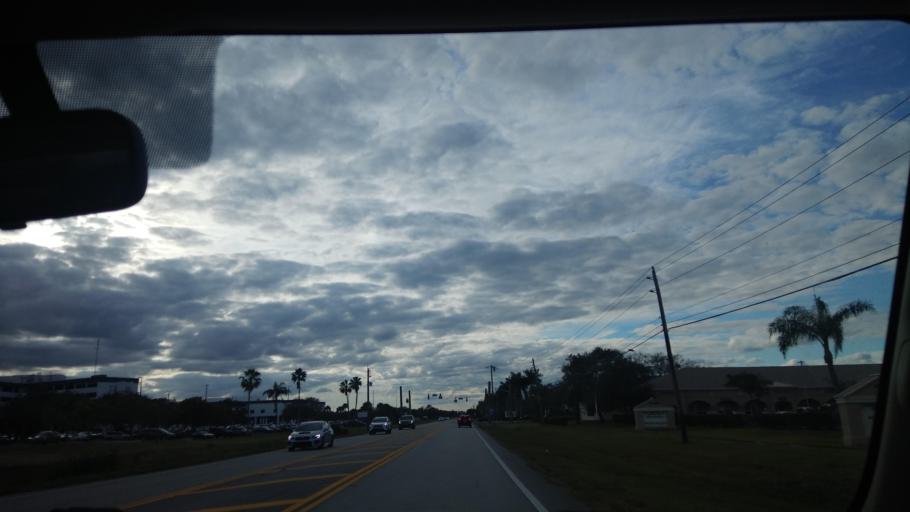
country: US
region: Florida
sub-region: Indian River County
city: Vero Beach
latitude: 27.6603
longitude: -80.3911
